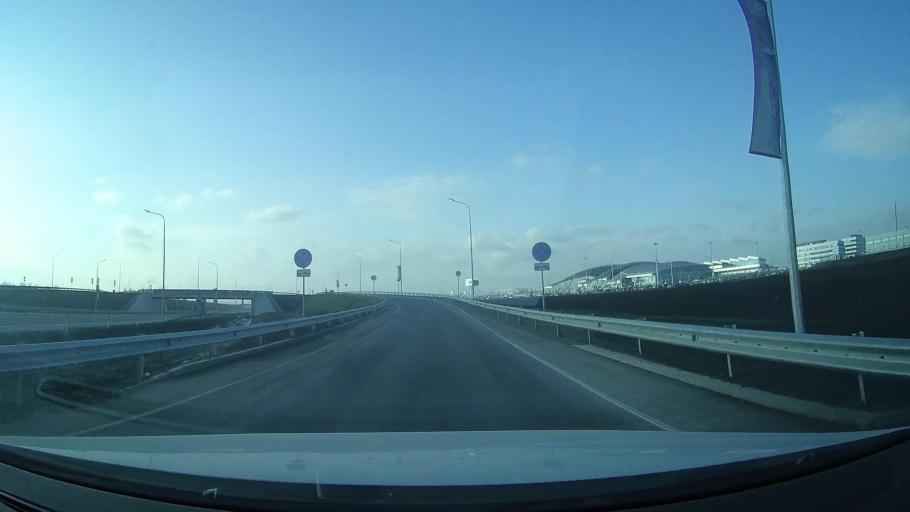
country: RU
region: Rostov
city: Grushevskaya
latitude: 47.4875
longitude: 39.9375
